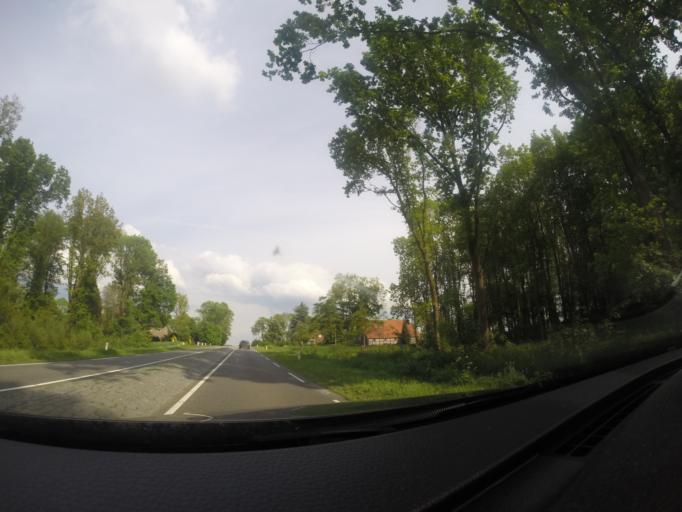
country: NL
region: Flevoland
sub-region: Gemeente Noordoostpolder
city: Ens
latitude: 52.6379
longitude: 5.7717
